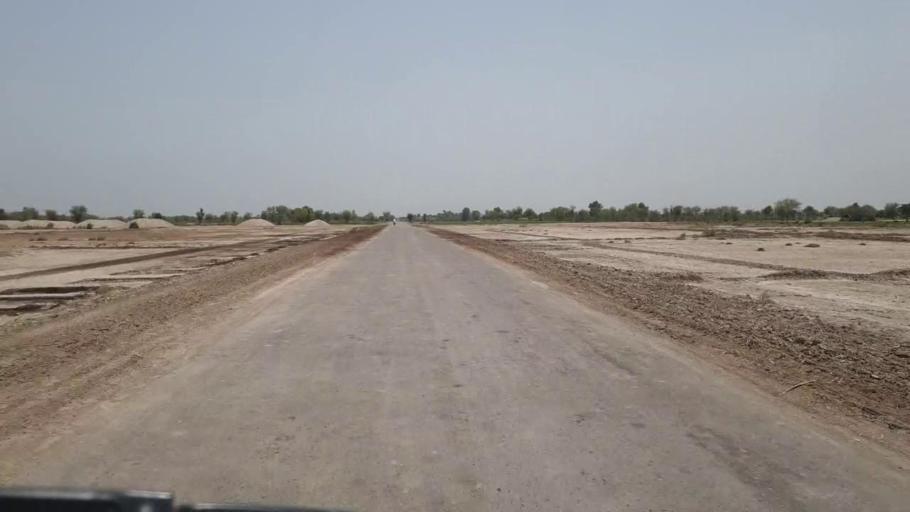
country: PK
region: Sindh
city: Daulatpur
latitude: 26.4510
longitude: 68.1172
